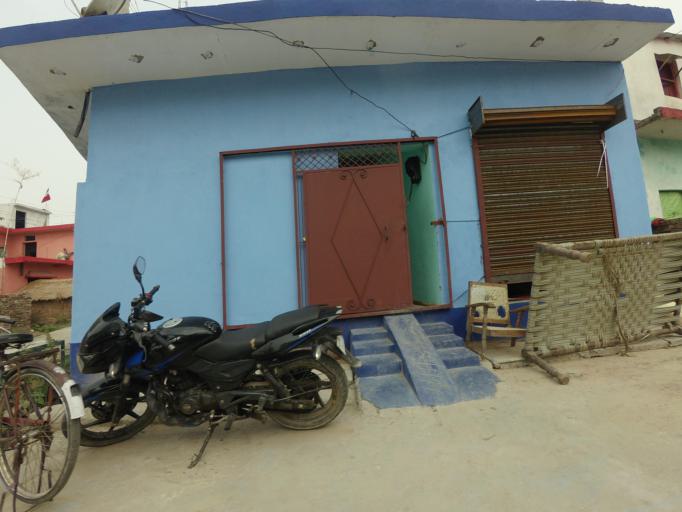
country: NP
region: Western Region
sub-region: Lumbini Zone
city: Bhairahawa
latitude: 27.4830
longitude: 83.4232
